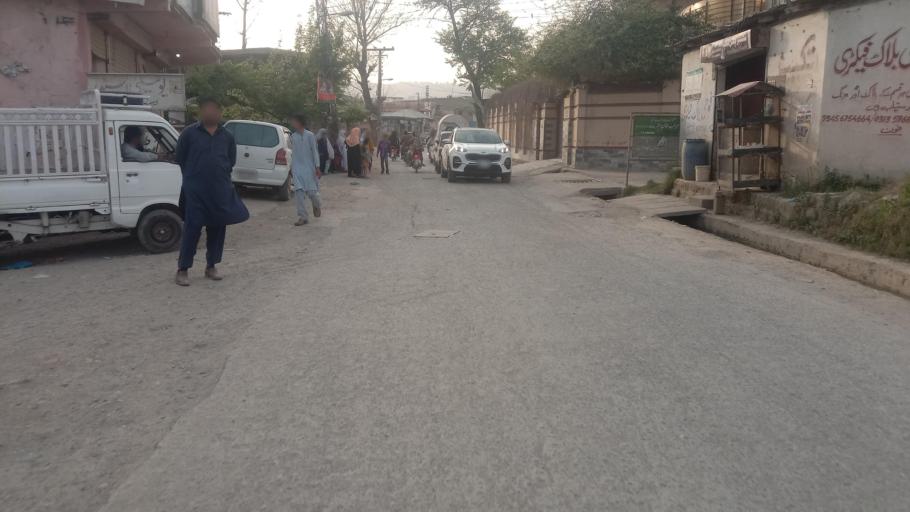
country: PK
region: Khyber Pakhtunkhwa
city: Abbottabad
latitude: 34.1738
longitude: 73.2451
